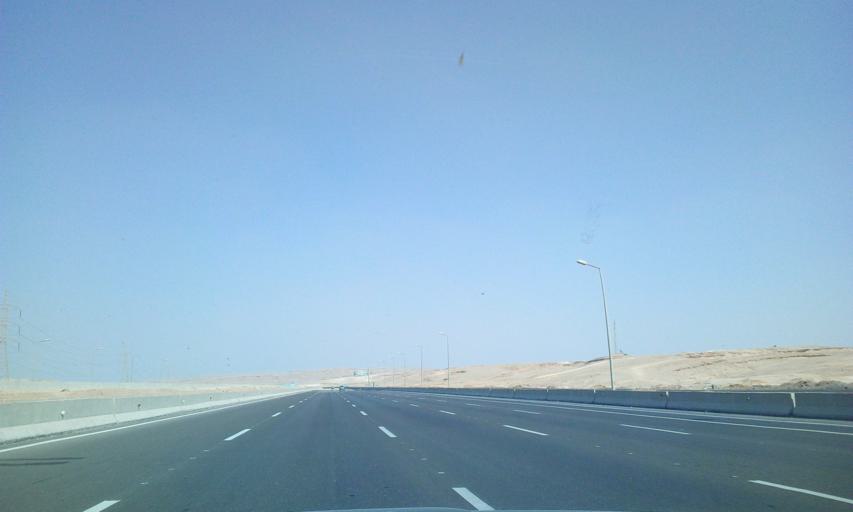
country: EG
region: As Suways
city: Ain Sukhna
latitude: 29.7619
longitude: 31.9718
